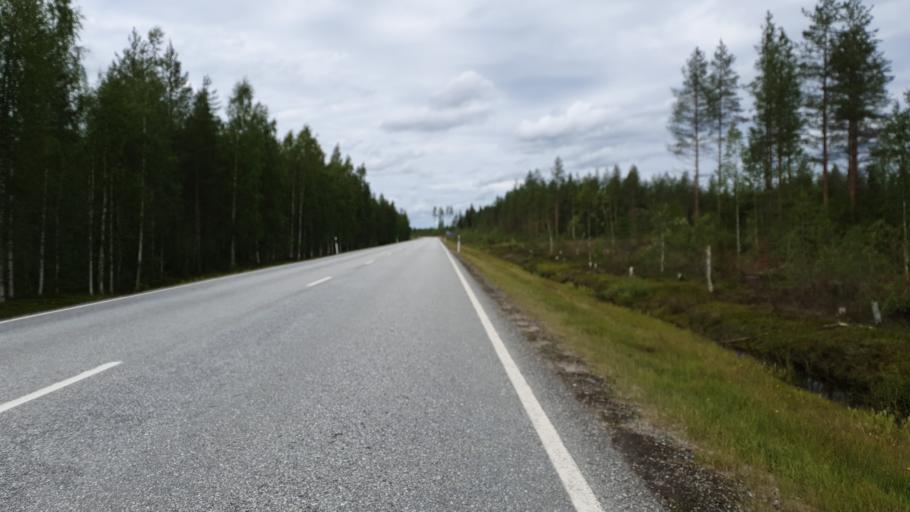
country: FI
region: Kainuu
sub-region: Kehys-Kainuu
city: Kuhmo
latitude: 64.4803
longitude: 29.7513
